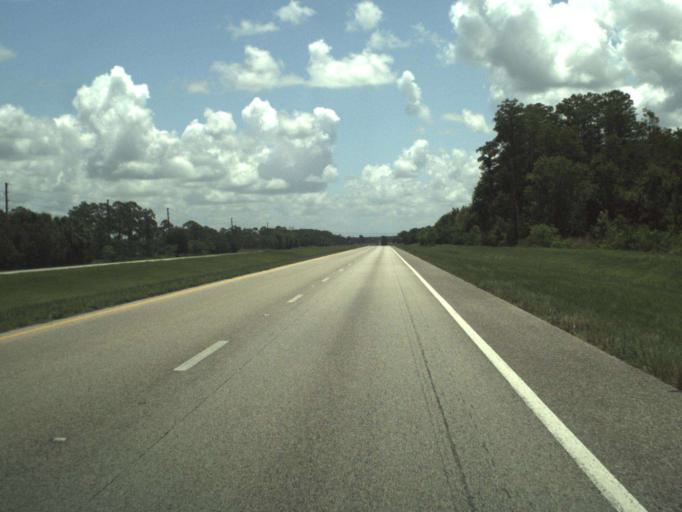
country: US
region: Florida
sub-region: Indian River County
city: Fellsmere
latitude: 27.6814
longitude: -80.8547
